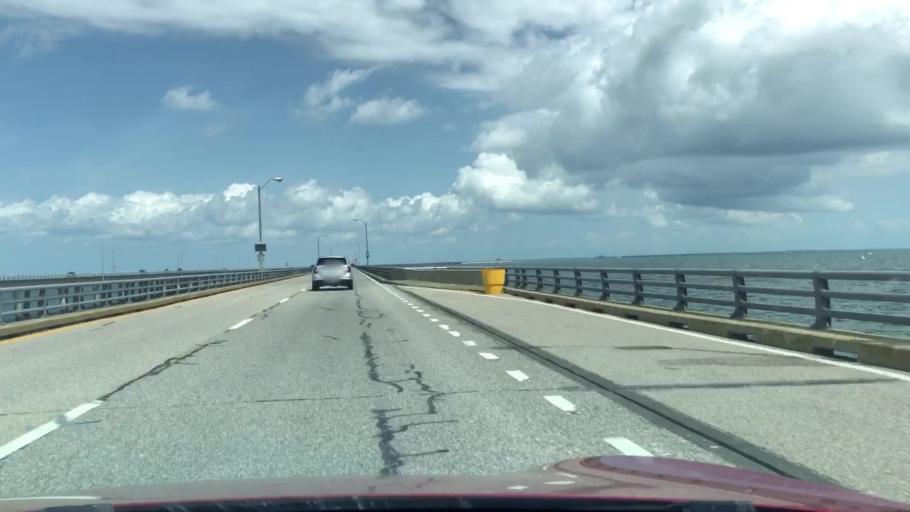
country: US
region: Virginia
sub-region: City of Virginia Beach
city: Virginia Beach
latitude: 37.0098
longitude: -76.0946
